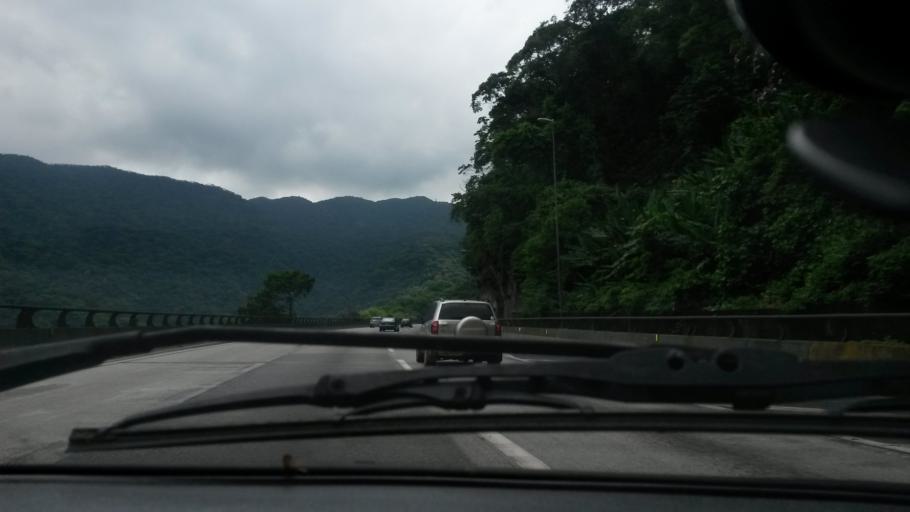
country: BR
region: Sao Paulo
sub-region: Cubatao
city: Cubatao
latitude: -23.8963
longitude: -46.4938
